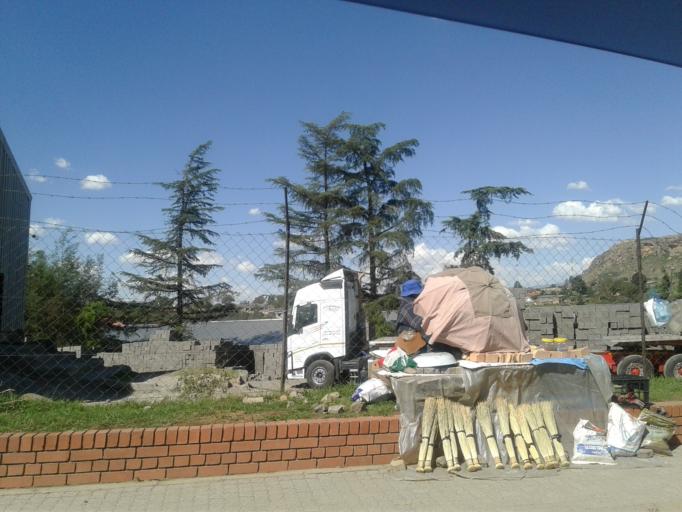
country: LS
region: Butha-Buthe
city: Butha-Buthe
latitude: -28.7676
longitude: 28.2501
